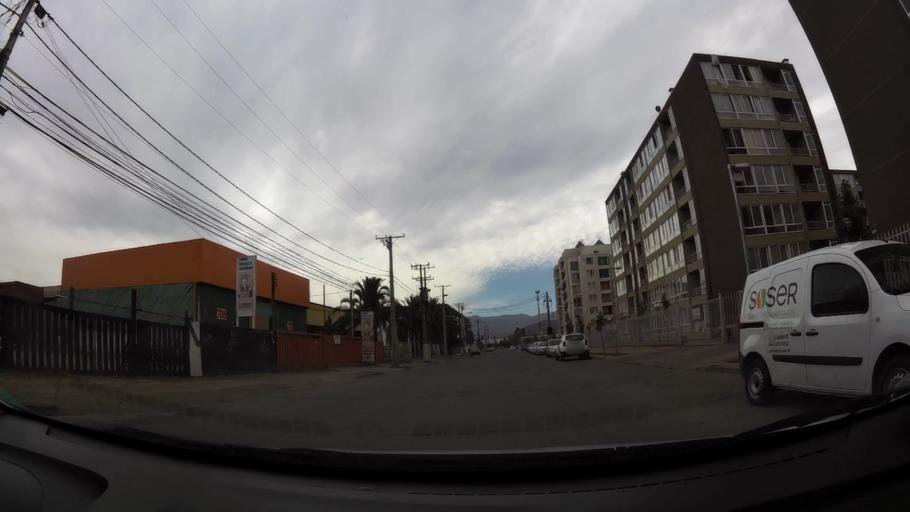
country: CL
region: O'Higgins
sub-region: Provincia de Cachapoal
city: Rancagua
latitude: -34.1405
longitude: -70.7382
